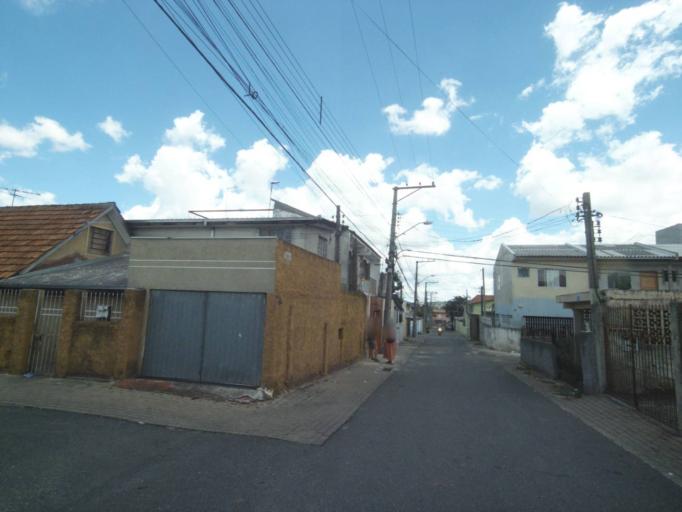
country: BR
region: Parana
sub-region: Curitiba
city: Curitiba
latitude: -25.5098
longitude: -49.3237
